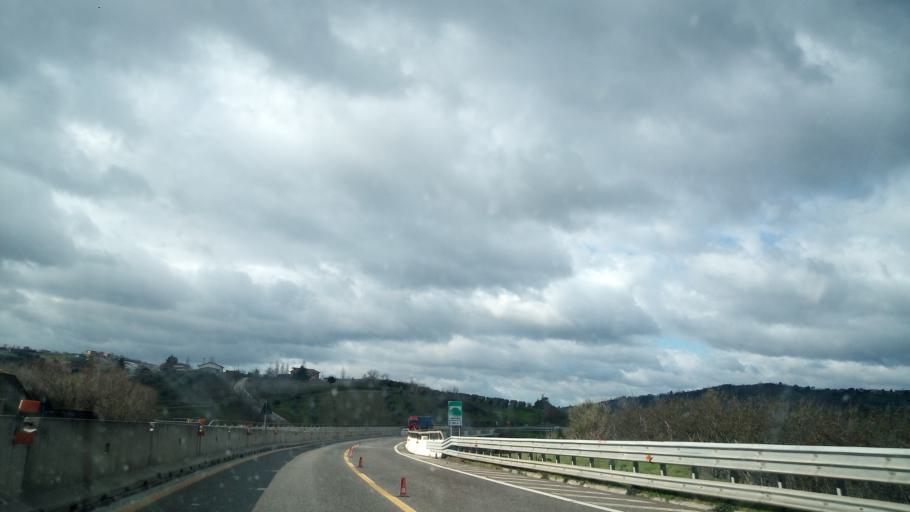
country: IT
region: Campania
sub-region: Provincia di Avellino
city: Flumeri
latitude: 41.0892
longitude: 15.1637
